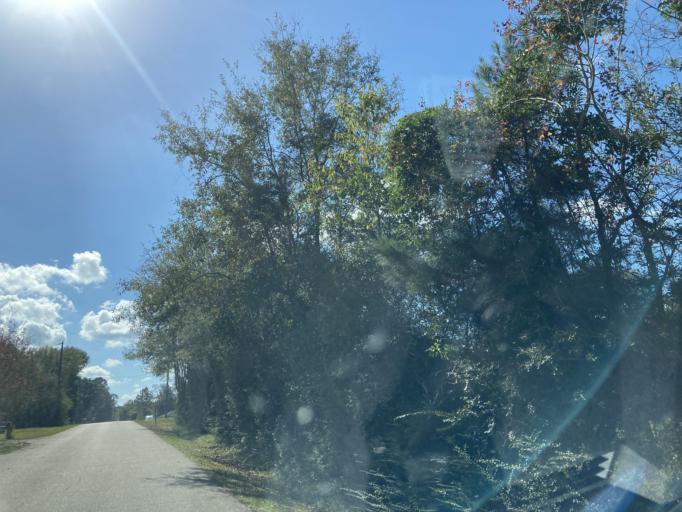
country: US
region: Mississippi
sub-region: Lamar County
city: West Hattiesburg
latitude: 31.2613
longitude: -89.4220
